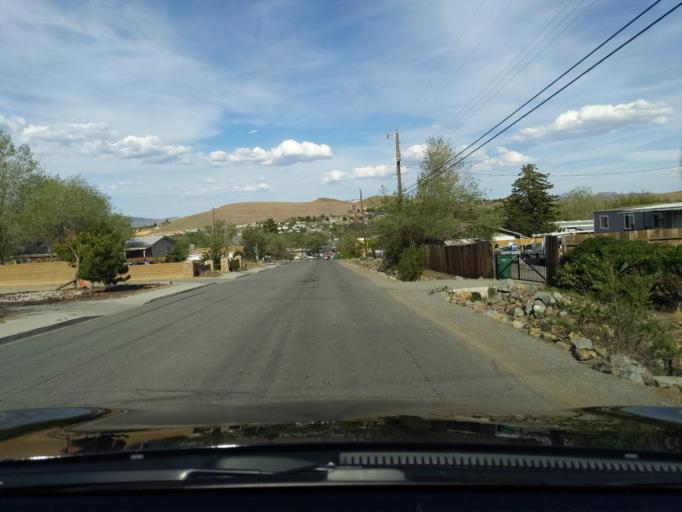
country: US
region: Nevada
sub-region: Washoe County
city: Sun Valley
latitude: 39.5819
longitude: -119.7840
